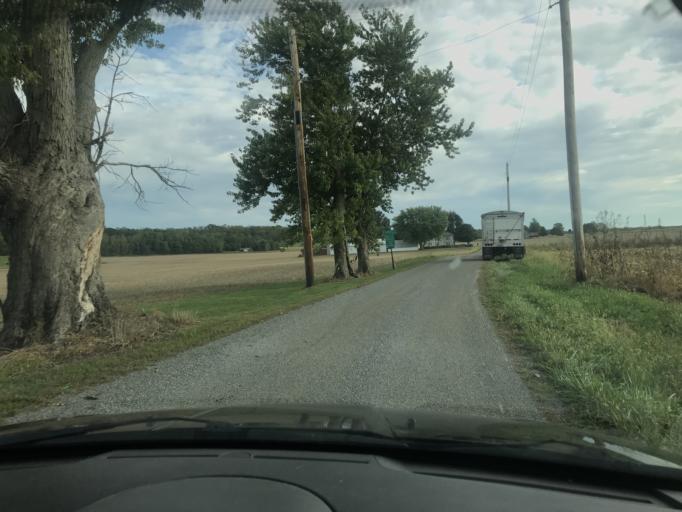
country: US
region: Ohio
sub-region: Logan County
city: West Liberty
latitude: 40.2398
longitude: -83.6868
